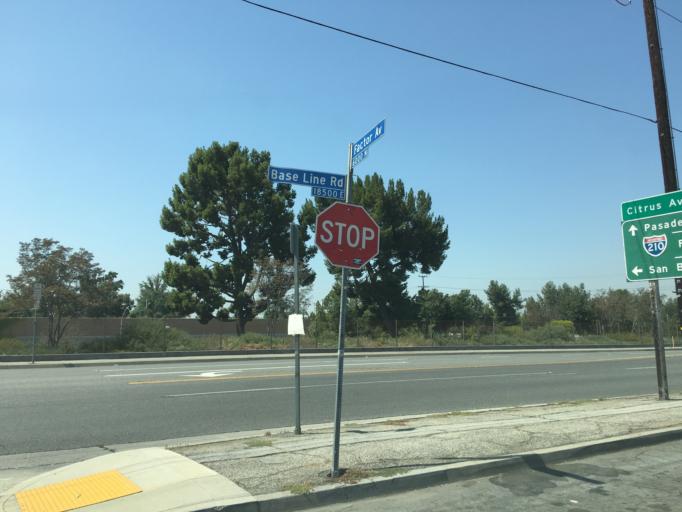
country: US
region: California
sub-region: Los Angeles County
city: Citrus
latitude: 34.1216
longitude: -117.8888
